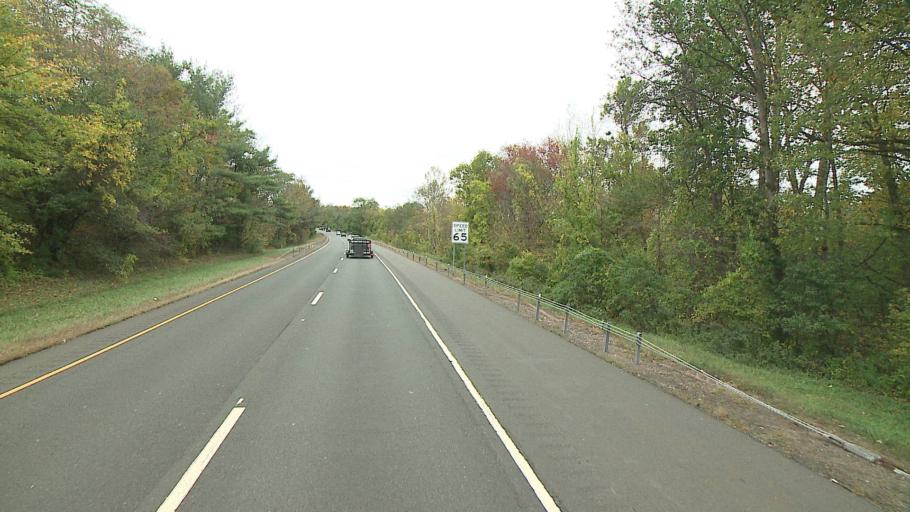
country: US
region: Connecticut
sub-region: Middlesex County
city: Higganum
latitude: 41.4802
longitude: -72.5599
